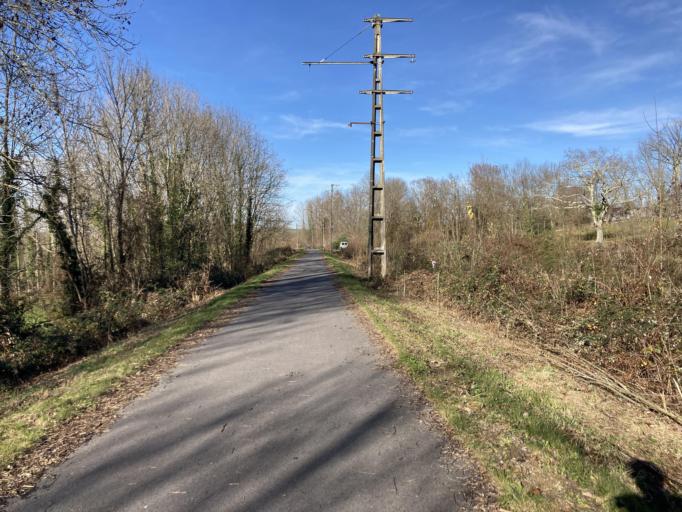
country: FR
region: Aquitaine
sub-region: Departement des Pyrenees-Atlantiques
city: Arudy
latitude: 43.1371
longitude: -0.4472
